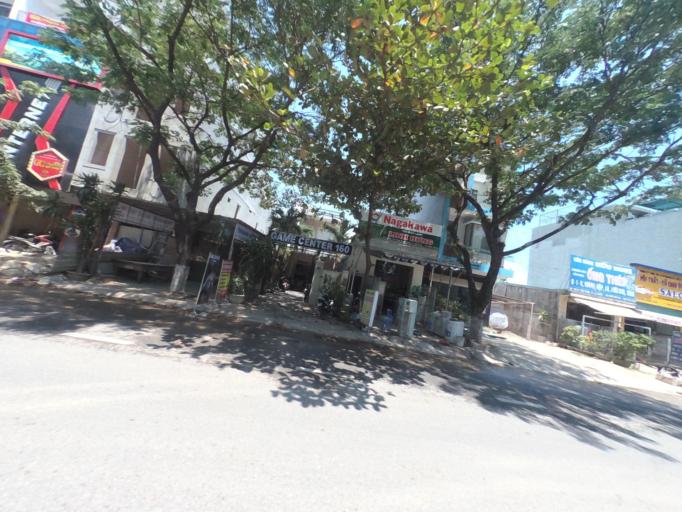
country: VN
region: Da Nang
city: Lien Chieu
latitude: 16.0707
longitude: 108.1727
